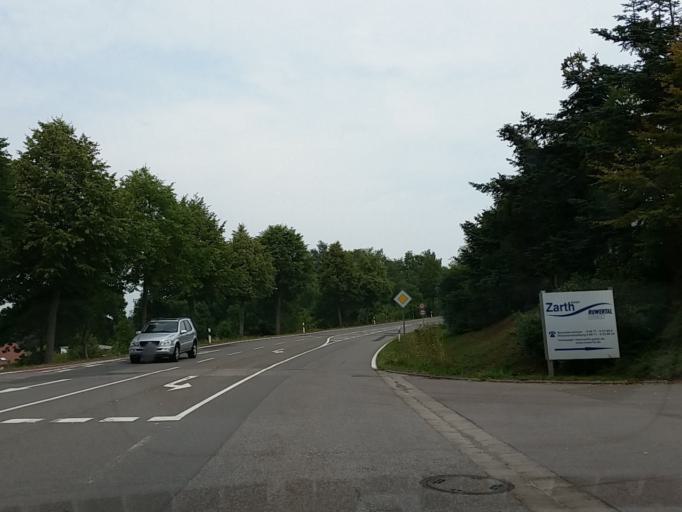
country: DE
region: Saarland
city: Wadern
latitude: 49.5396
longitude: 6.8972
